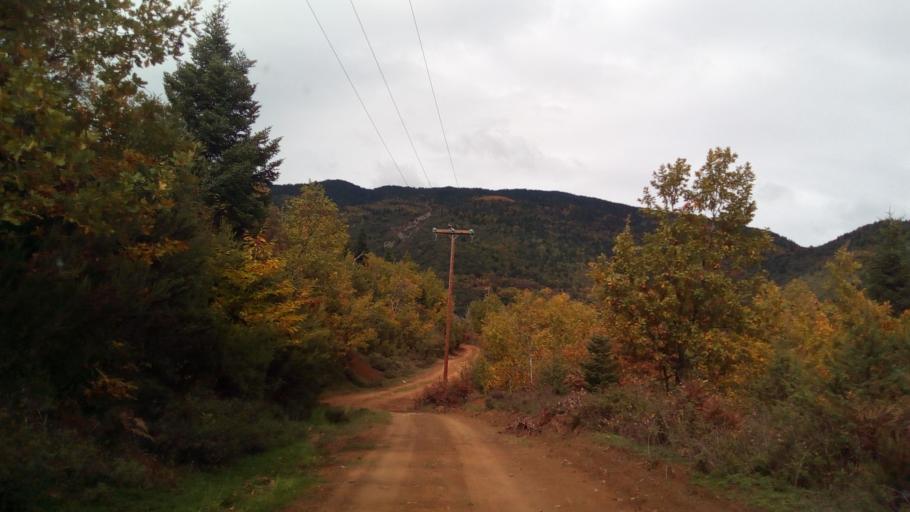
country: GR
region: West Greece
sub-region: Nomos Aitolias kai Akarnanias
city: Nafpaktos
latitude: 38.5569
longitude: 21.9658
